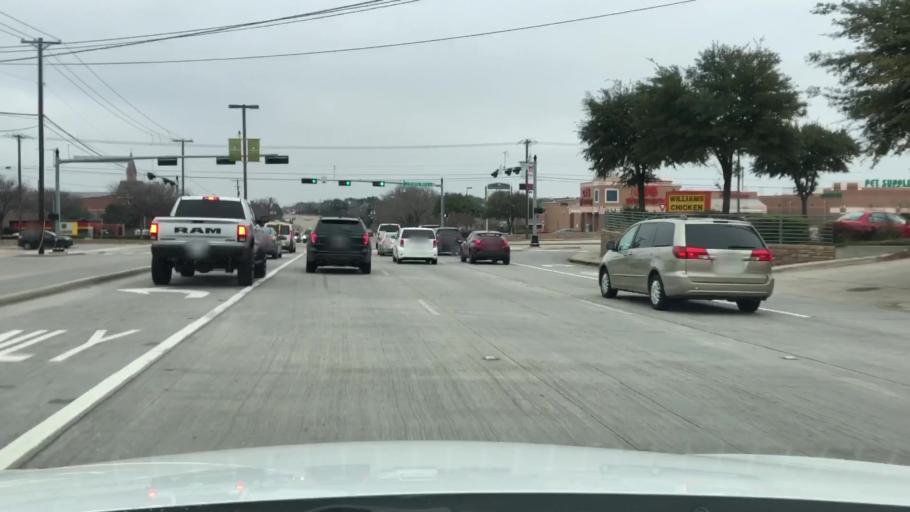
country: US
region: Texas
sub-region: Dallas County
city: Addison
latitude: 32.9863
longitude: -96.8548
